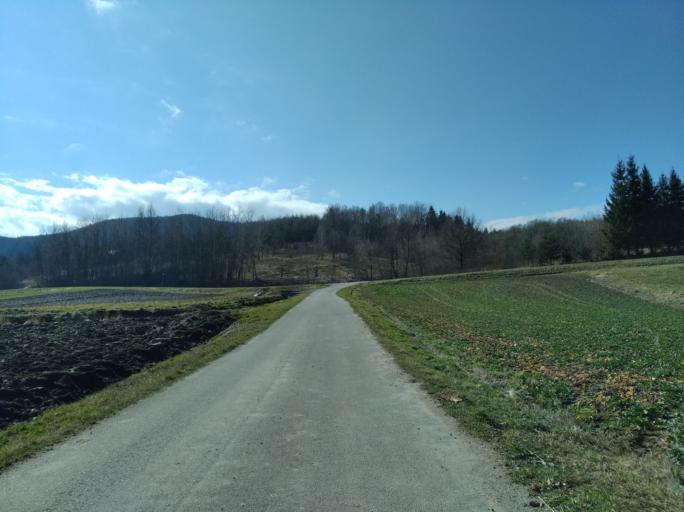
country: PL
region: Subcarpathian Voivodeship
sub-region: Powiat strzyzowski
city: Wysoka Strzyzowska
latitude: 49.8019
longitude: 21.7524
